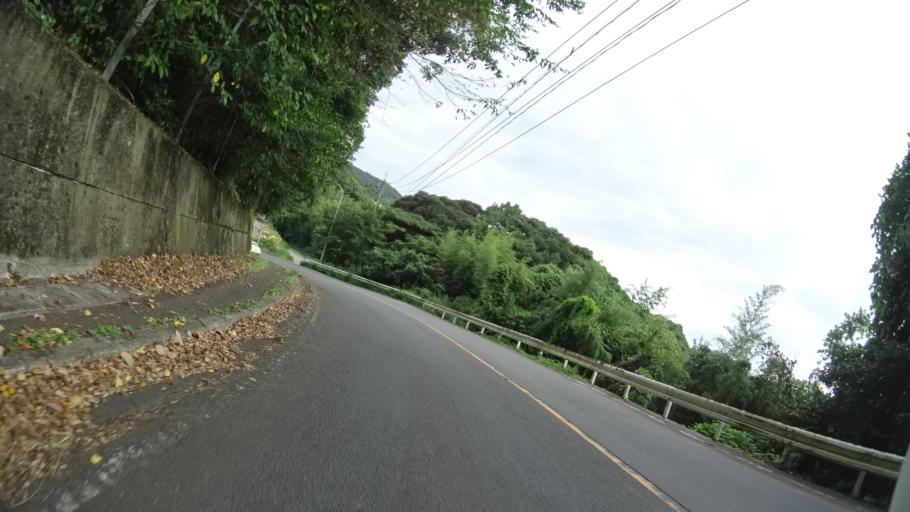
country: JP
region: Oita
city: Beppu
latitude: 33.3256
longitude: 131.4776
